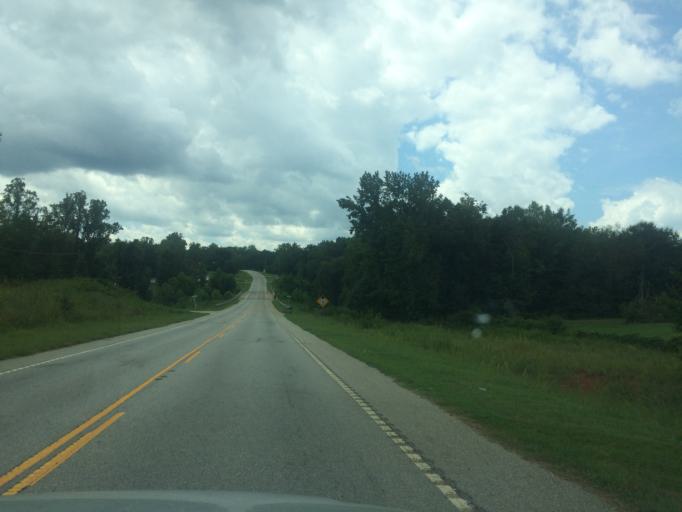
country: US
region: South Carolina
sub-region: Spartanburg County
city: Inman
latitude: 35.1408
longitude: -82.0394
